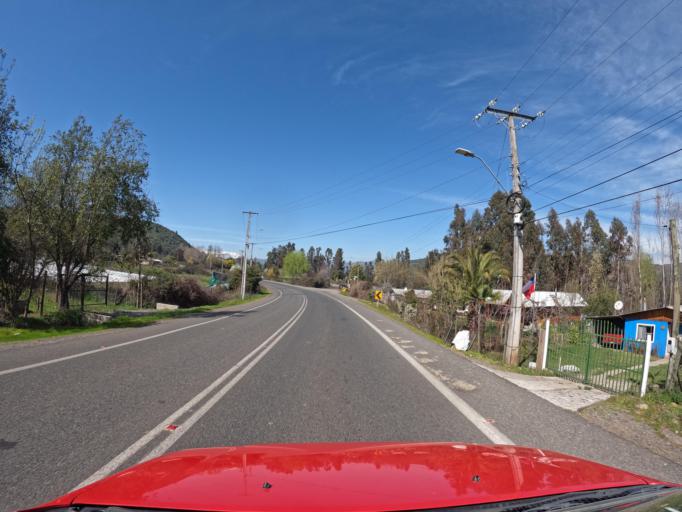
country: CL
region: Maule
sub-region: Provincia de Curico
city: Teno
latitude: -34.9784
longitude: -70.9928
